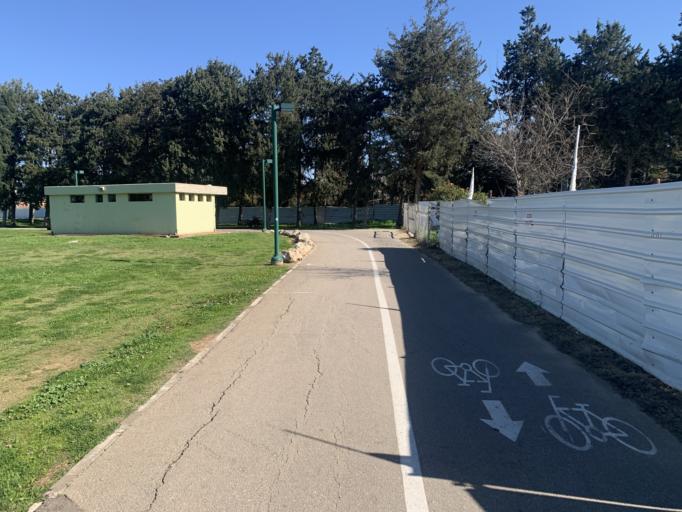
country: IL
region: Tel Aviv
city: Ramat Gan
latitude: 32.1007
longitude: 34.8183
